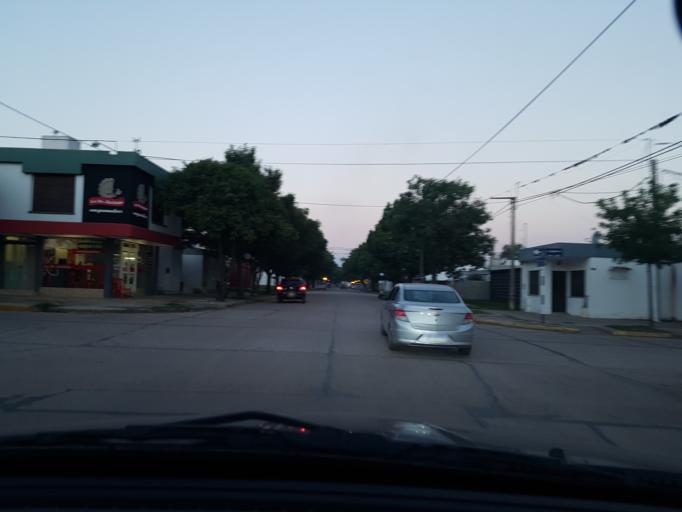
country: AR
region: Cordoba
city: General Cabrera
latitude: -32.7584
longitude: -63.7950
